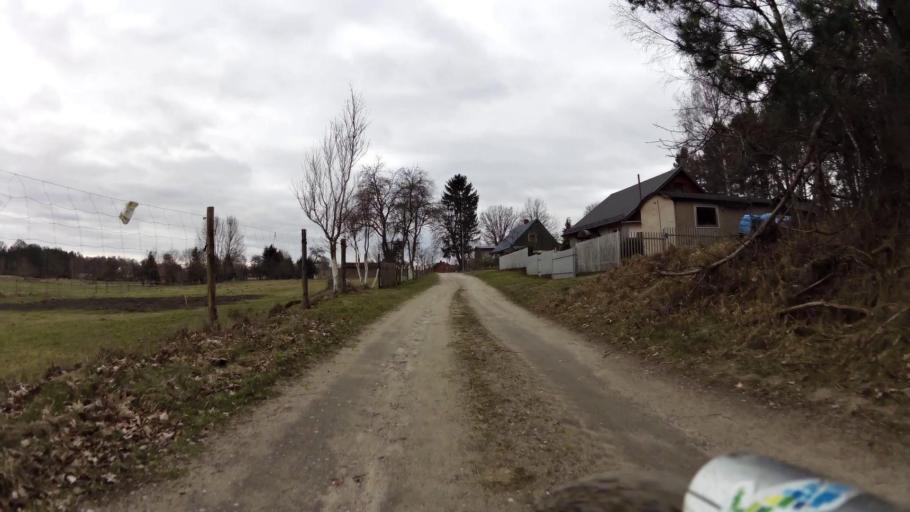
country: PL
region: Pomeranian Voivodeship
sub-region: Powiat bytowski
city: Trzebielino
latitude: 54.1085
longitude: 17.1301
